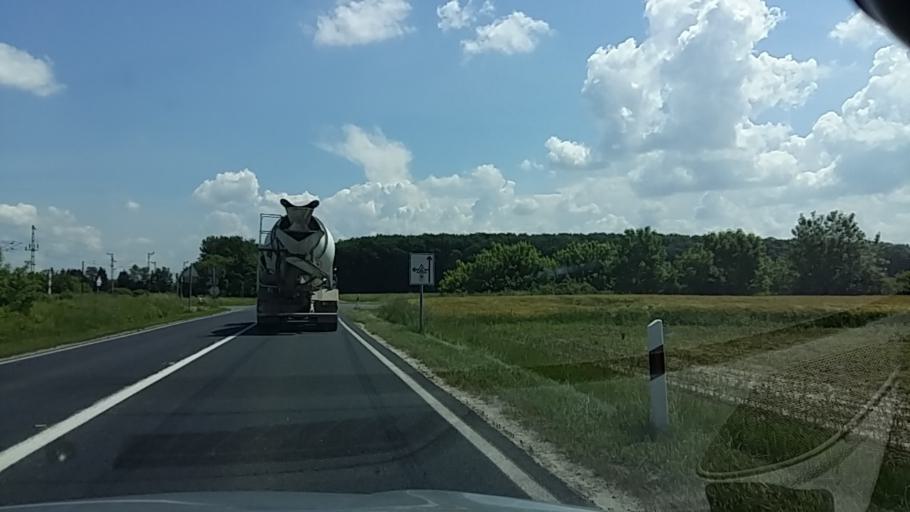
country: AT
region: Burgenland
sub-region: Politischer Bezirk Gussing
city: Moschendorf
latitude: 46.9739
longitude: 16.4860
